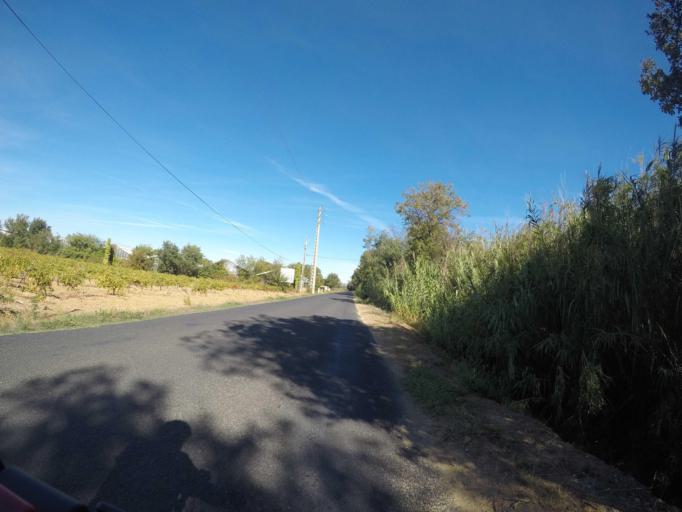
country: FR
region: Languedoc-Roussillon
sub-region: Departement des Pyrenees-Orientales
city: Le Soler
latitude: 42.6583
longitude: 2.7972
